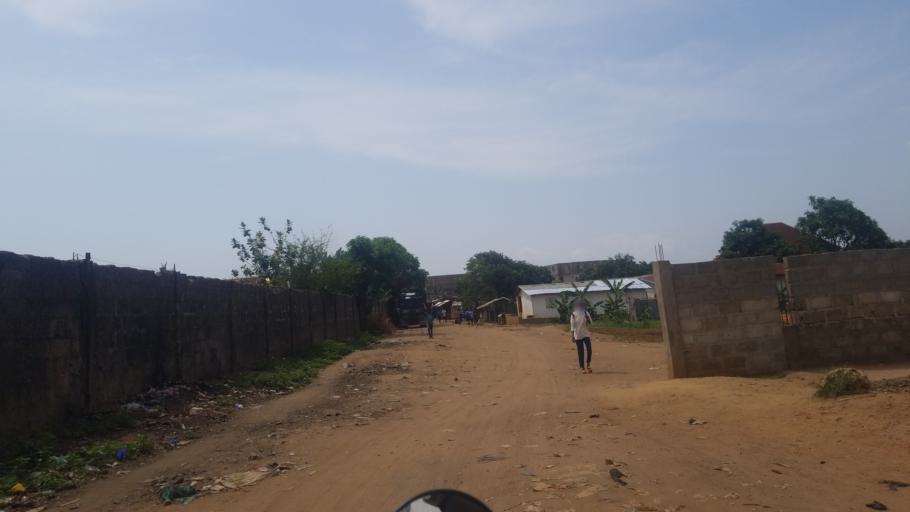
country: SL
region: Western Area
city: Waterloo
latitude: 8.3292
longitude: -13.0490
